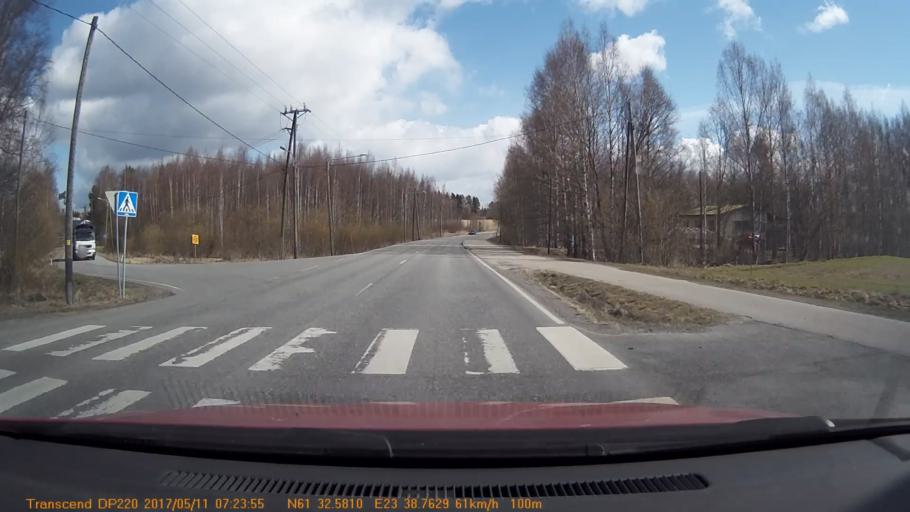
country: FI
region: Pirkanmaa
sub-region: Tampere
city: Yloejaervi
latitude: 61.5431
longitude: 23.6462
